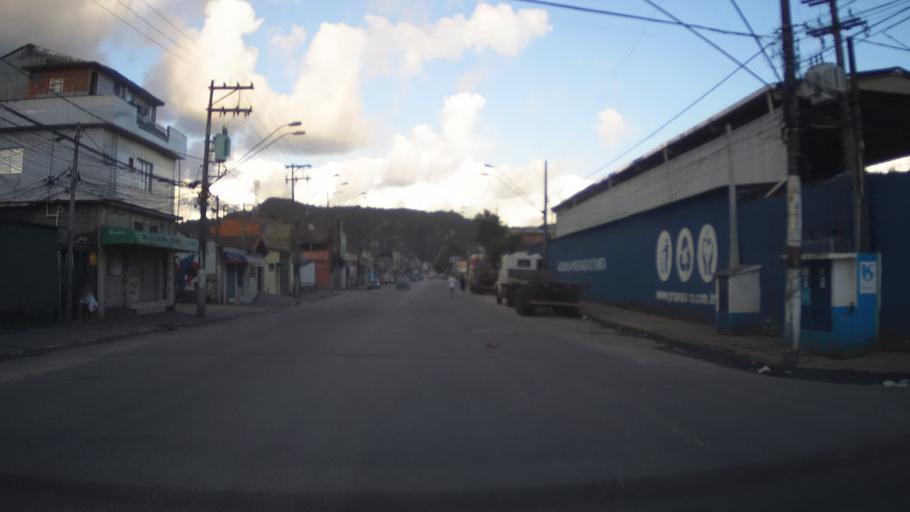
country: BR
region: Sao Paulo
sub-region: Sao Vicente
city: Sao Vicente
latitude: -23.9508
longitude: -46.3841
